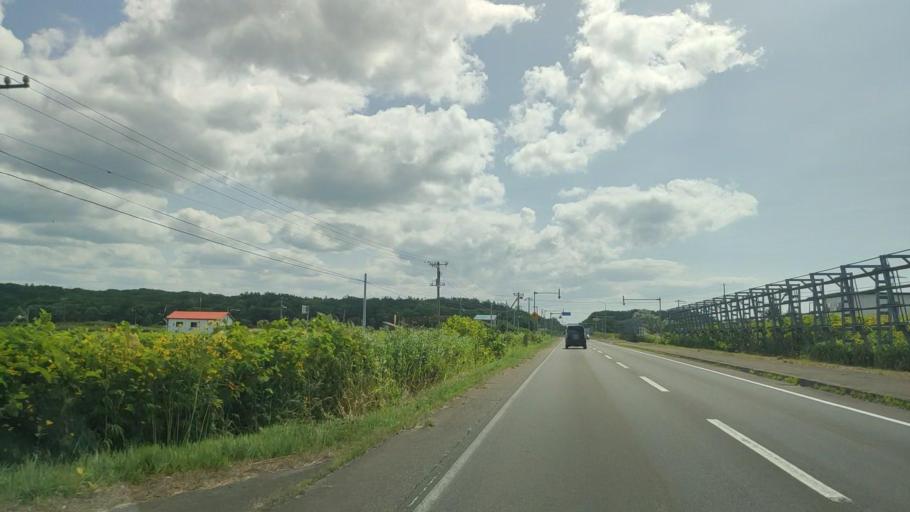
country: JP
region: Hokkaido
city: Makubetsu
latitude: 44.7718
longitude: 141.7923
